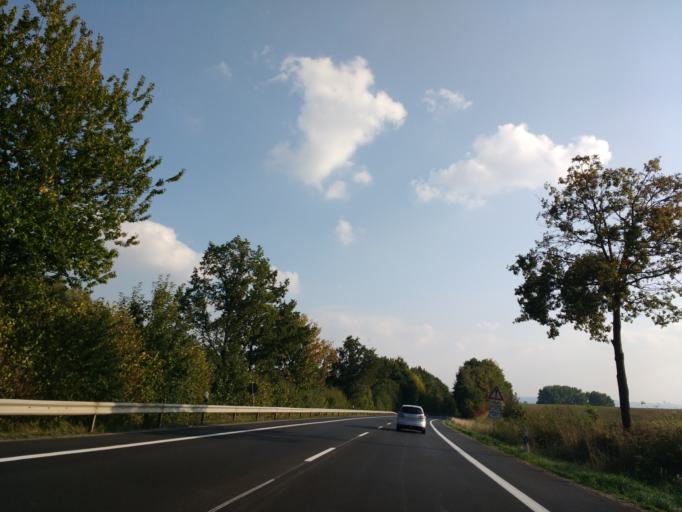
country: DE
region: North Rhine-Westphalia
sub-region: Regierungsbezirk Detmold
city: Steinheim
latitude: 51.9067
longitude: 9.0864
